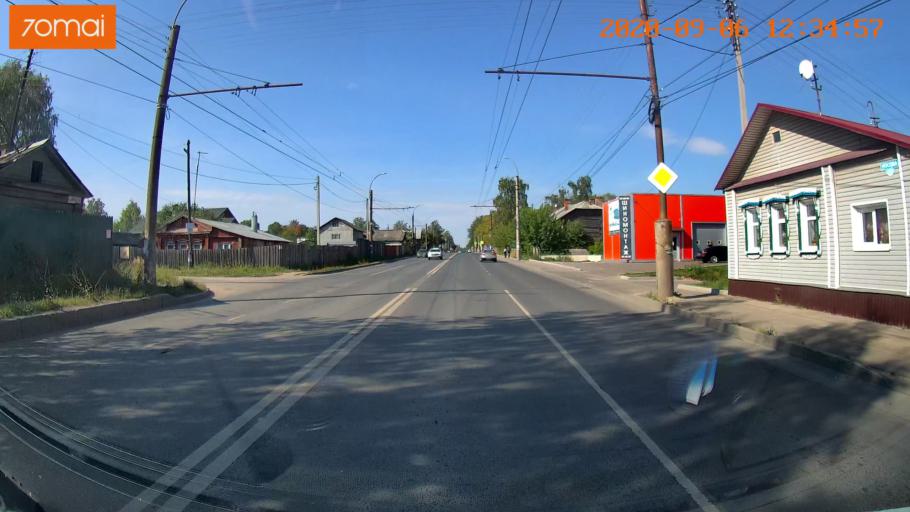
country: RU
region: Ivanovo
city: Bogorodskoye
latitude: 57.0181
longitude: 40.9985
